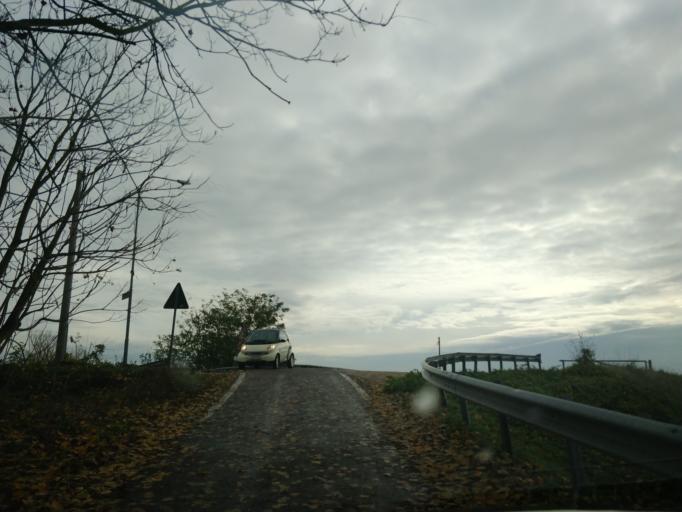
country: IT
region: Emilia-Romagna
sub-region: Provincia di Bologna
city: Padulle
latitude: 44.6357
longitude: 11.3054
